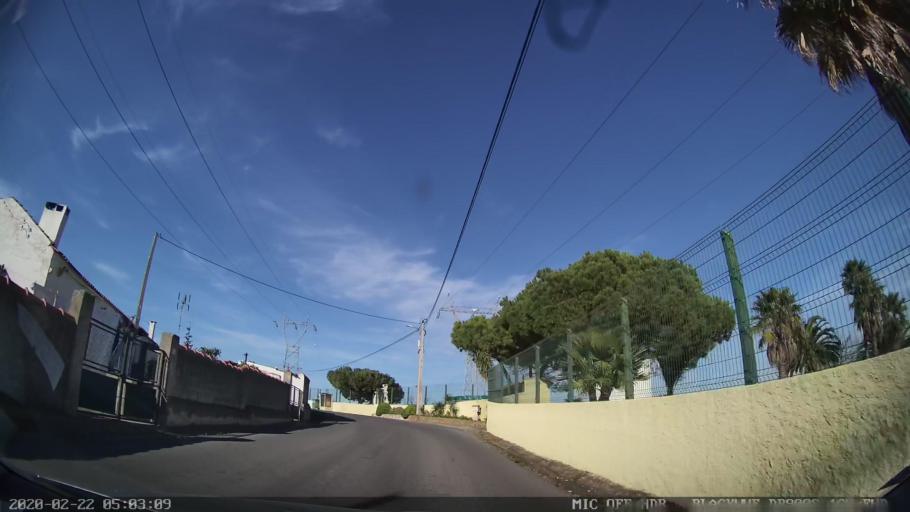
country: PT
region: Lisbon
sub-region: Vila Franca de Xira
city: Vila Franca de Xira
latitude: 38.9685
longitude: -8.9951
